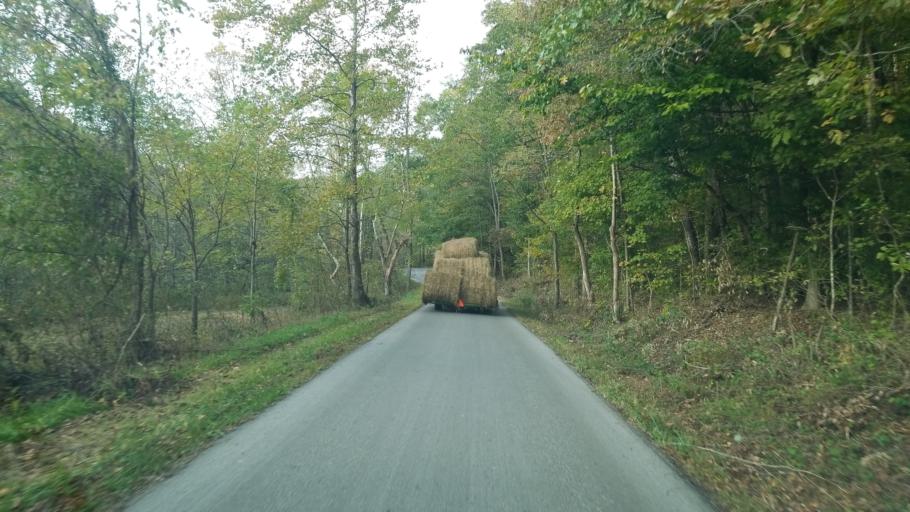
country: US
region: Kentucky
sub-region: Lewis County
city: Vanceburg
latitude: 38.5012
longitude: -83.4832
